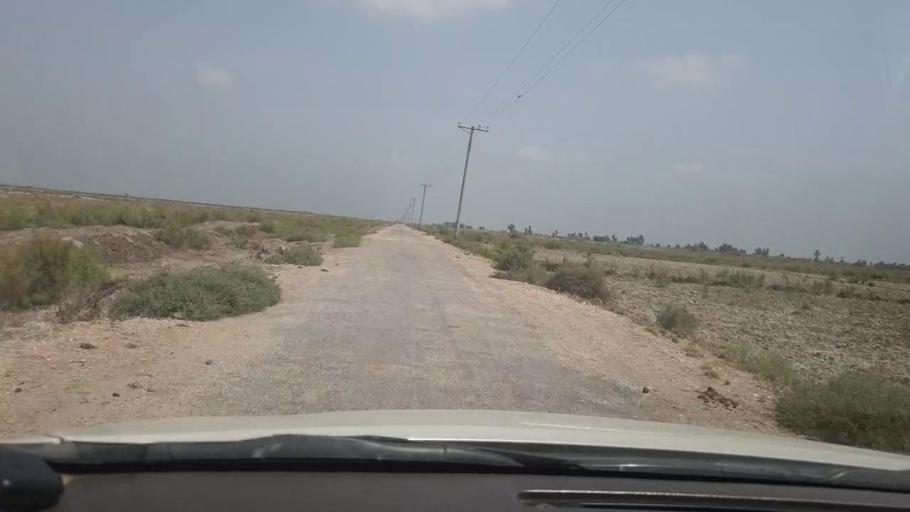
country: PK
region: Sindh
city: Garhi Yasin
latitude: 27.9895
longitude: 68.5016
